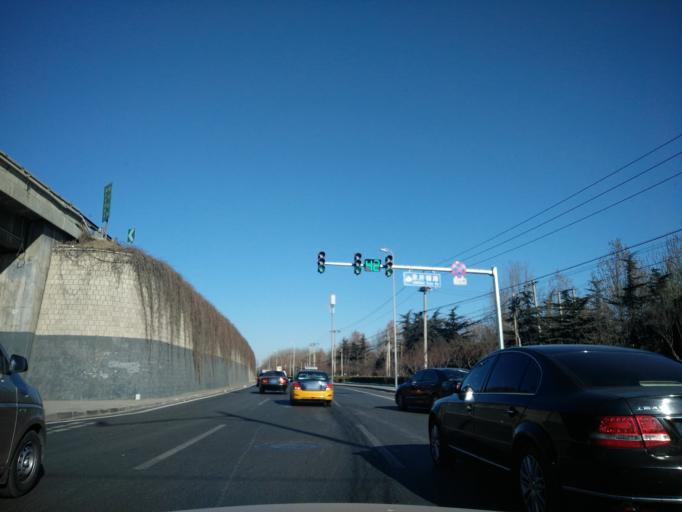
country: CN
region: Beijing
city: Xihongmen
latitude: 39.7890
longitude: 116.3427
